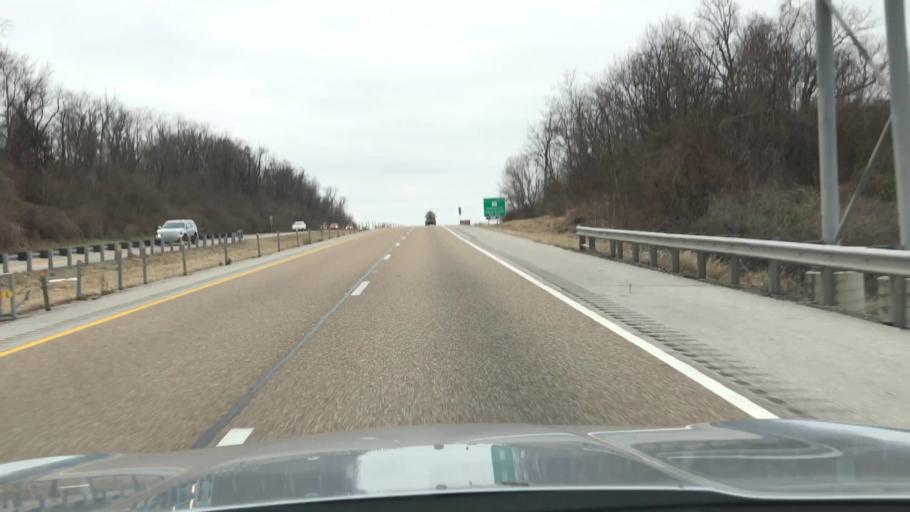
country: US
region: Illinois
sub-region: Madison County
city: Collinsville
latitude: 38.6840
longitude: -90.0061
